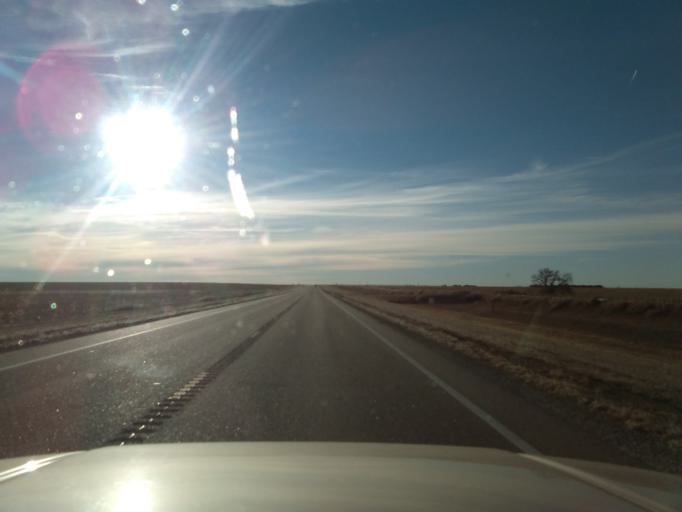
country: US
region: Kansas
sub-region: Sheridan County
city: Hoxie
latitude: 39.5192
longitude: -100.6255
